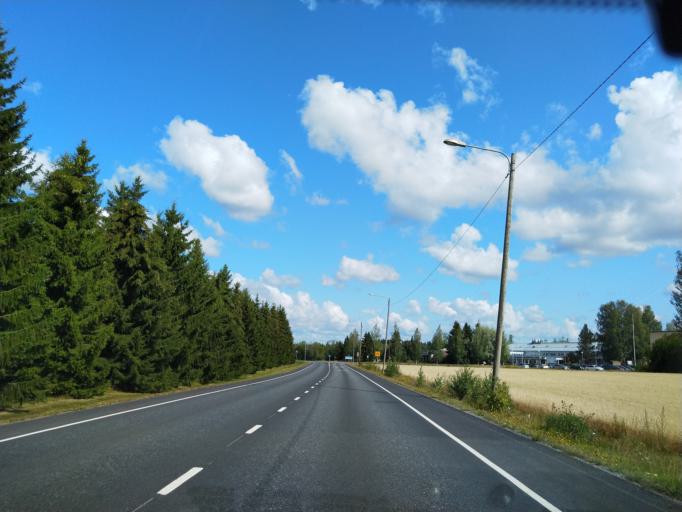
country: FI
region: Satakunta
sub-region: Pori
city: Huittinen
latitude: 61.1775
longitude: 22.7124
